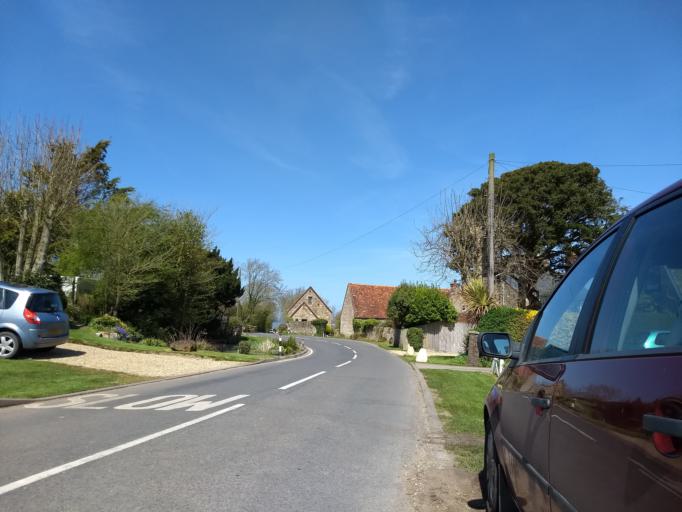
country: GB
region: England
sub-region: Isle of Wight
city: Gurnard
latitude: 50.7459
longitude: -1.3330
